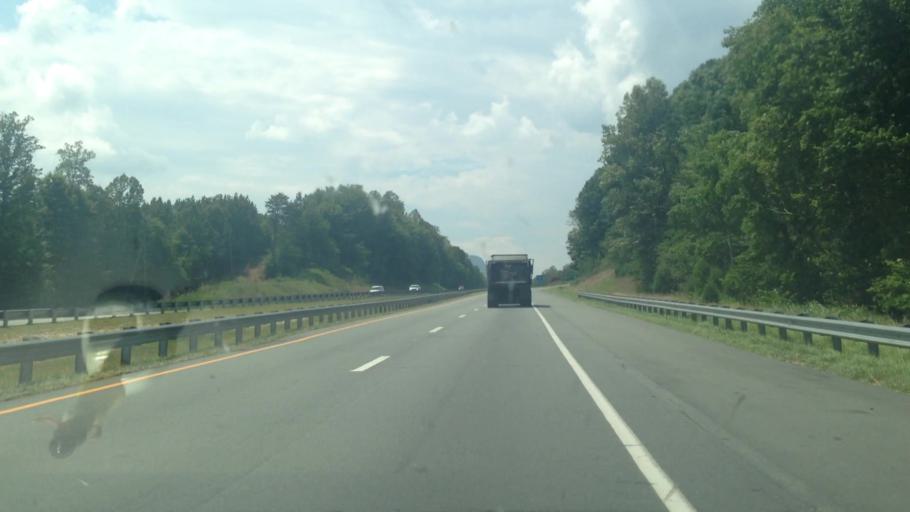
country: US
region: North Carolina
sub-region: Stokes County
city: King
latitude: 36.3033
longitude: -80.4174
